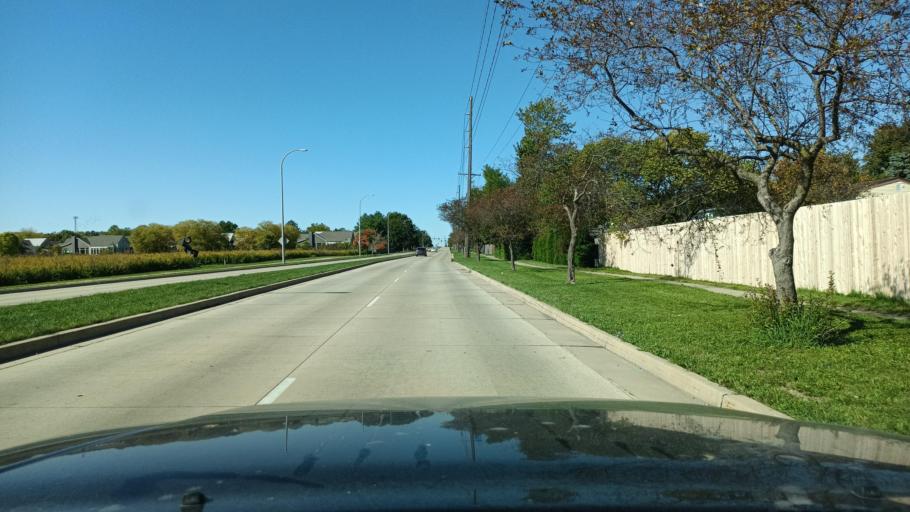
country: US
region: Illinois
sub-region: Champaign County
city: Urbana
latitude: 40.0838
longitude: -88.2024
